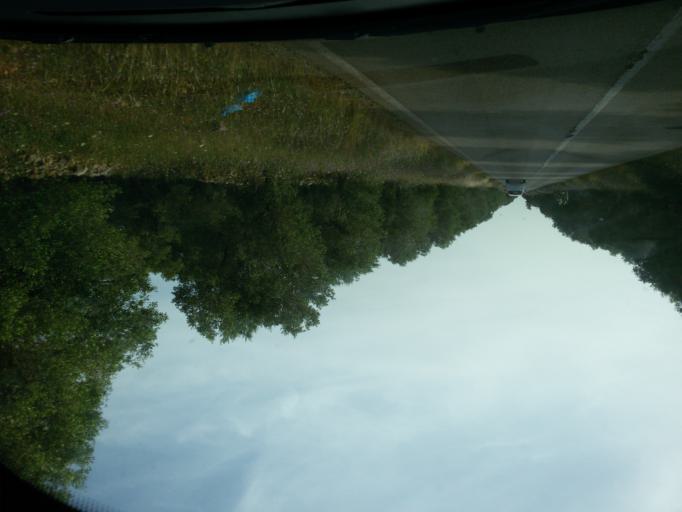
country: IT
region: Apulia
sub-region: Provincia di Brindisi
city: San Pancrazio Salentino
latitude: 40.3487
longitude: 17.8463
